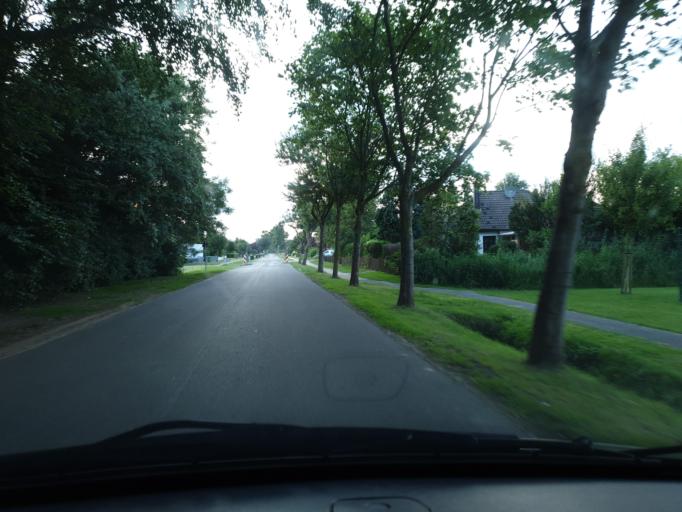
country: DE
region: Schleswig-Holstein
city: Friedrichskoog
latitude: 54.0040
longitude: 8.8754
